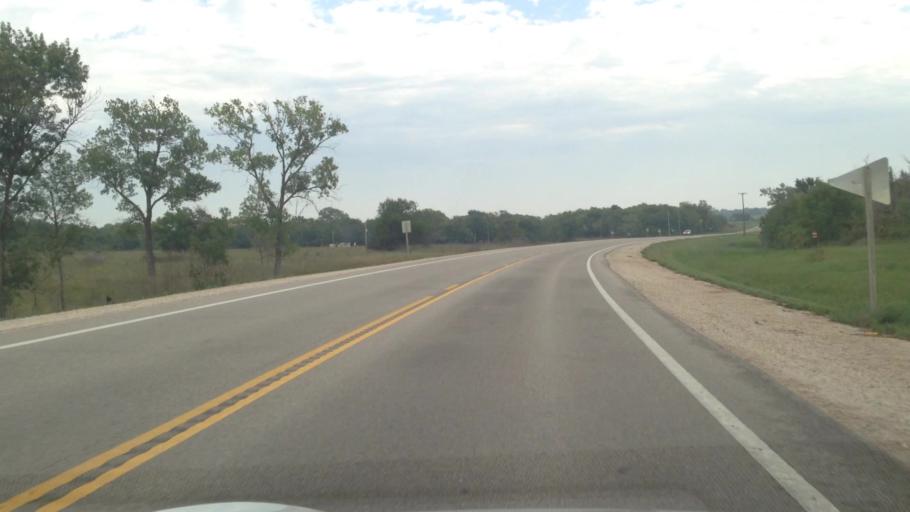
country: US
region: Kansas
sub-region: Allen County
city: Iola
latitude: 37.9080
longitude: -95.1022
